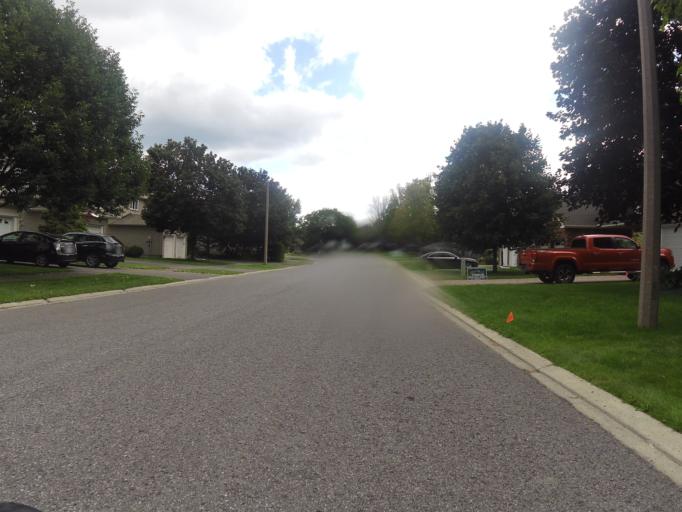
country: CA
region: Ontario
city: Bells Corners
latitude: 45.3212
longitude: -75.9136
